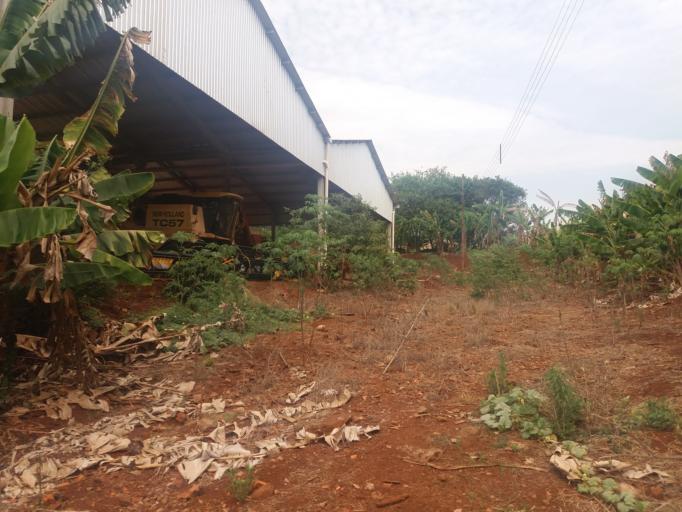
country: BR
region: Parana
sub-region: Londrina
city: Londrina
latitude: -23.5211
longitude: -51.1025
